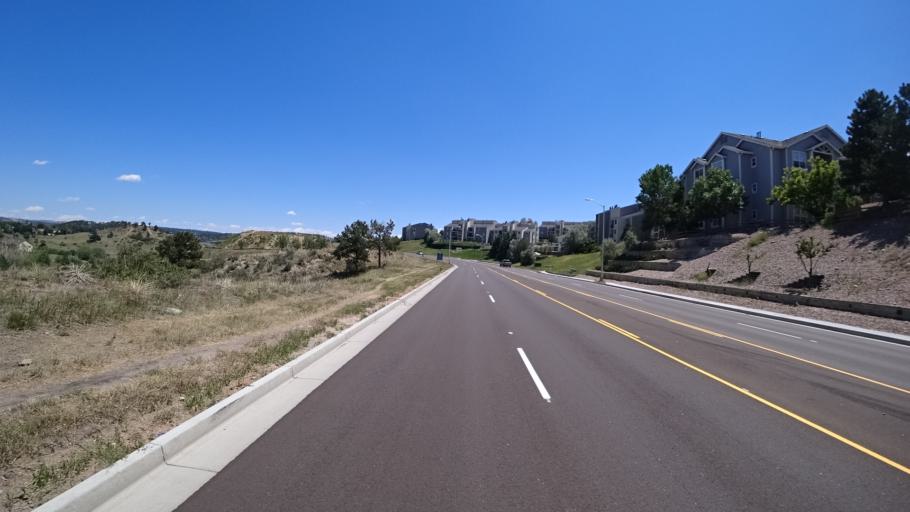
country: US
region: Colorado
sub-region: El Paso County
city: Air Force Academy
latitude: 38.9179
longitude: -104.8348
